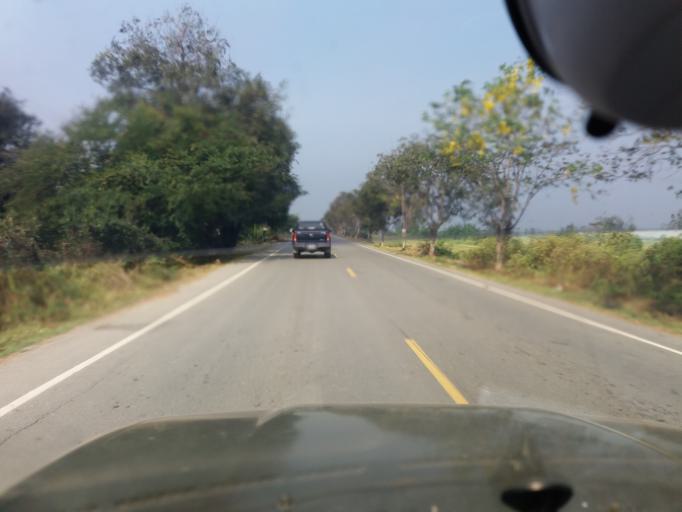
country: TH
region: Sing Buri
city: Bang Racham
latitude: 14.8750
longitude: 100.2861
